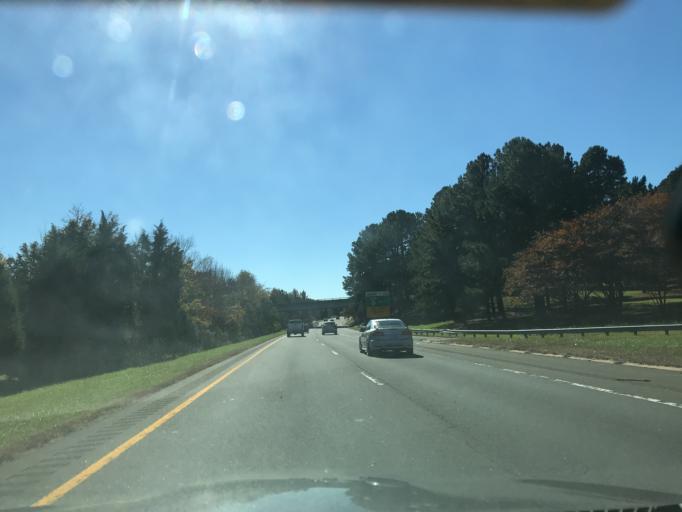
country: US
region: North Carolina
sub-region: Durham County
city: Durham
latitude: 35.9132
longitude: -78.8644
